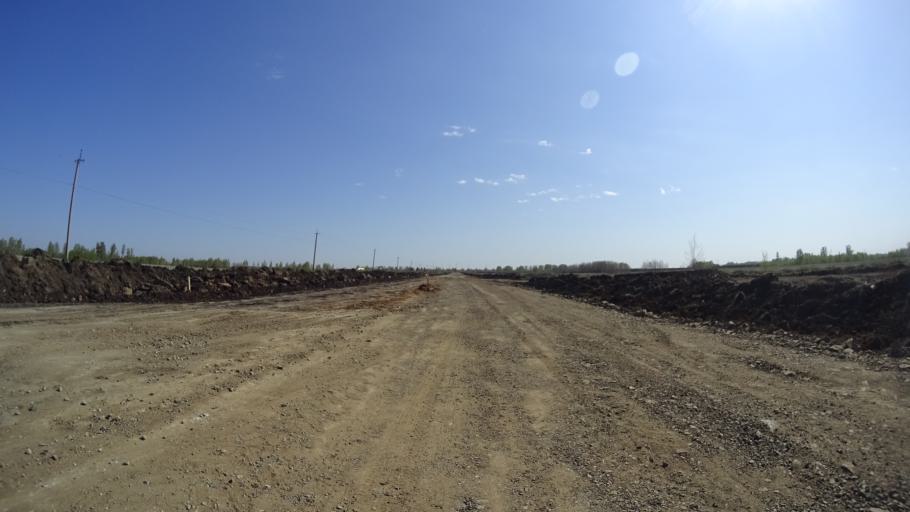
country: RU
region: Chelyabinsk
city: Troitsk
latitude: 54.1827
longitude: 61.4856
